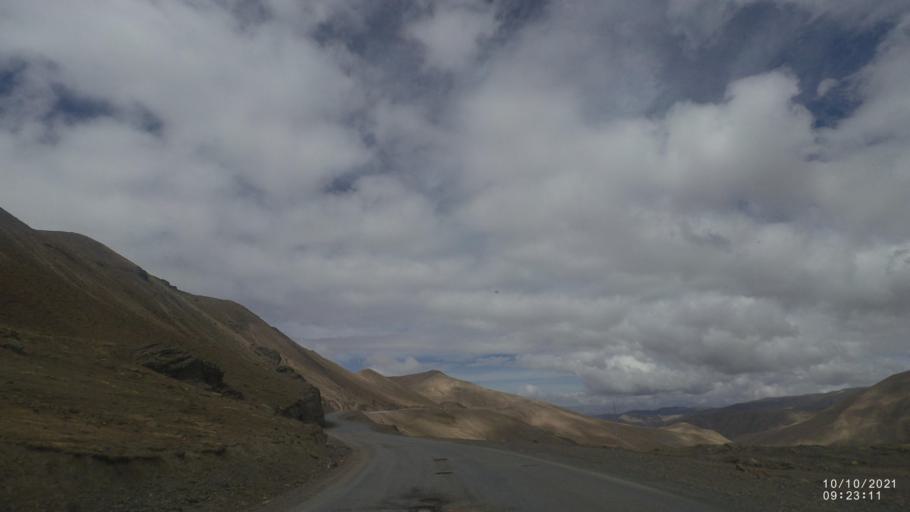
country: BO
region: La Paz
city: Quime
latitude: -17.0827
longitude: -67.3010
